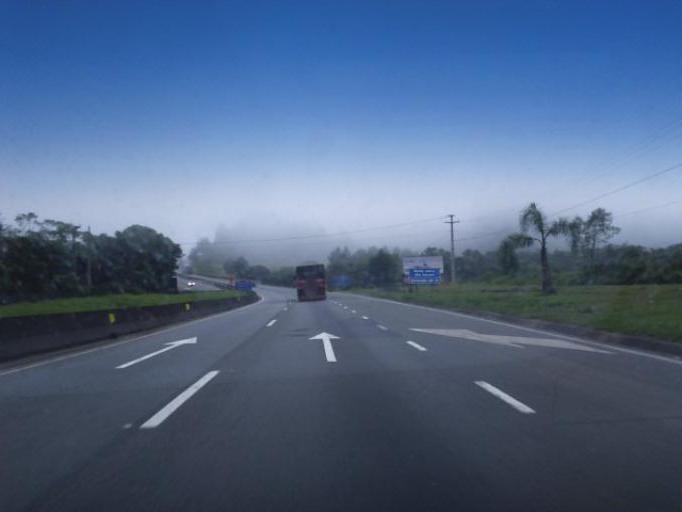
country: BR
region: Parana
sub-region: Sao Jose Dos Pinhais
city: Sao Jose dos Pinhais
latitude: -25.8527
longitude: -48.9746
